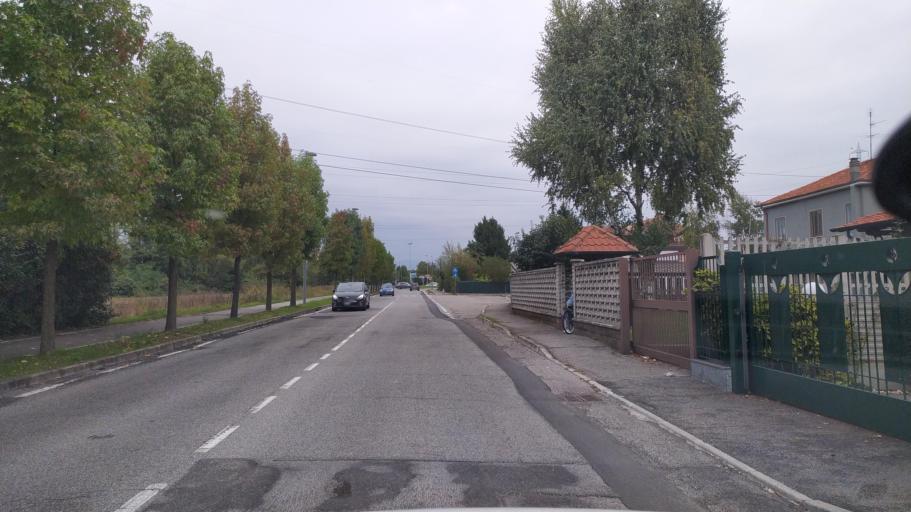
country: IT
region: Lombardy
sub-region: Provincia di Monza e Brianza
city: Desio
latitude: 45.6293
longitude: 9.1976
